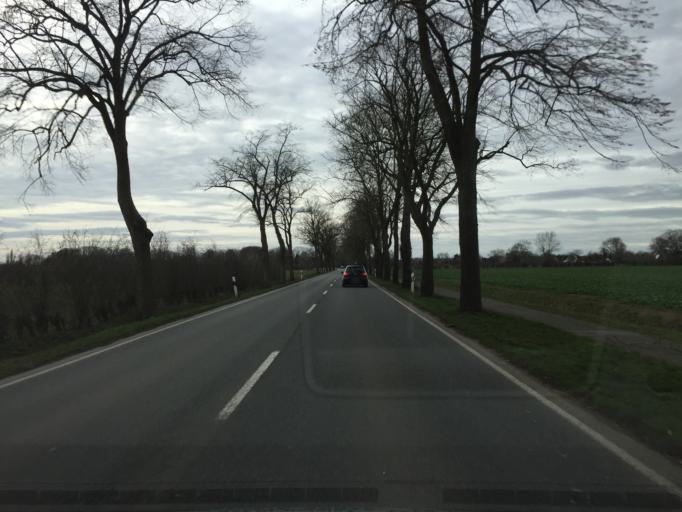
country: DE
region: Lower Saxony
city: Thedinghausen
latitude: 52.9641
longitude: 9.0387
